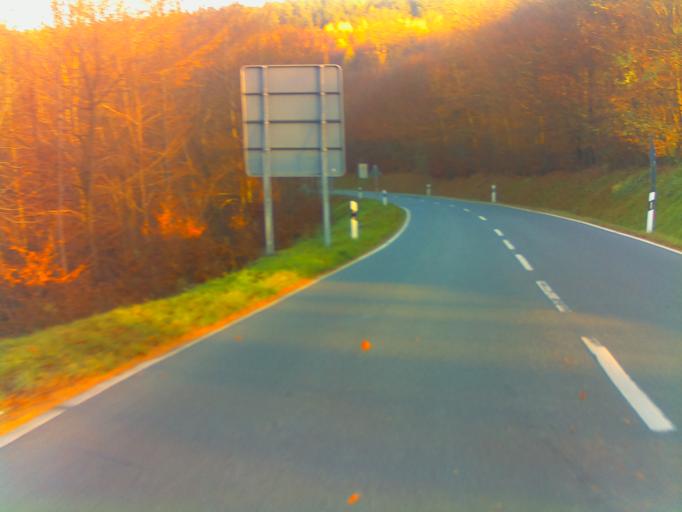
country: DE
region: Hesse
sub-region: Regierungsbezirk Darmstadt
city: Hesseneck
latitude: 49.5516
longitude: 9.1204
